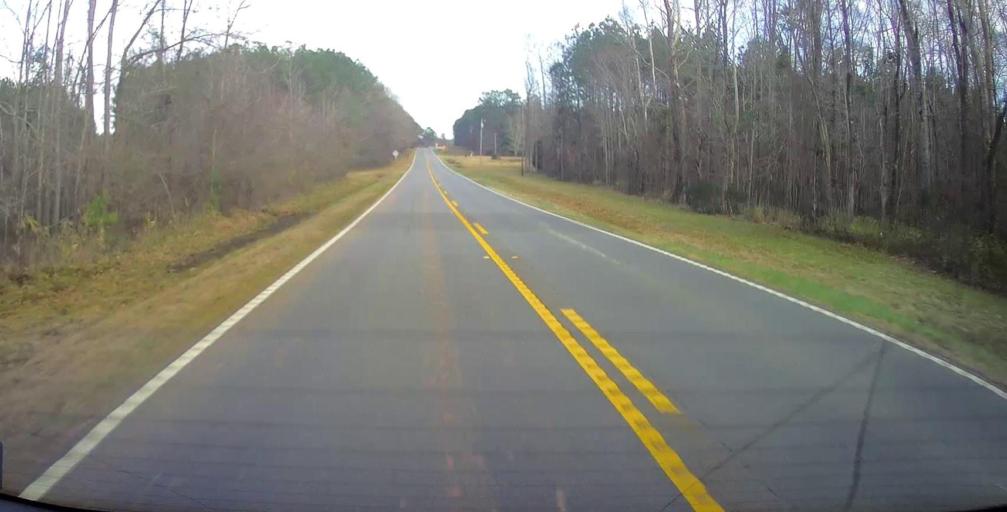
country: US
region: Georgia
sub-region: Harris County
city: Hamilton
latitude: 32.6979
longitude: -84.8078
